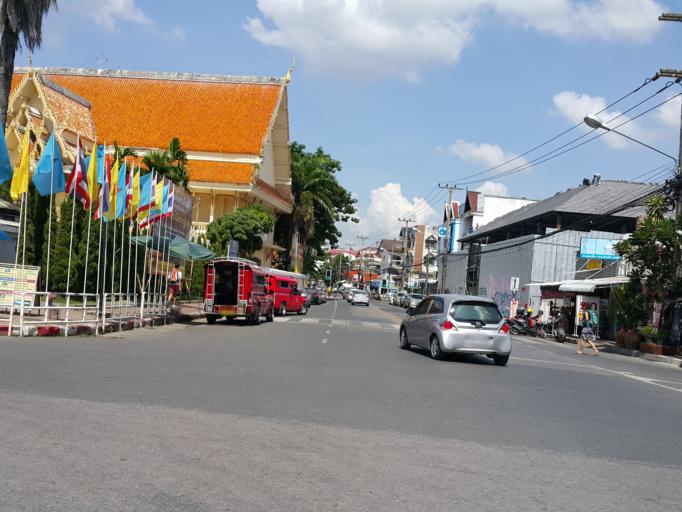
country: TH
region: Chiang Mai
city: Chiang Mai
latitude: 18.7885
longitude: 98.9825
